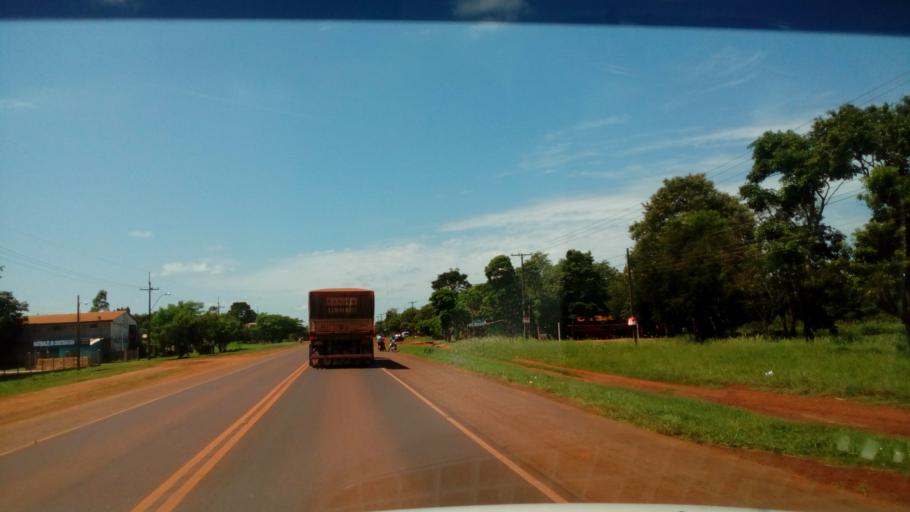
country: PY
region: Alto Parana
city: Colonia Yguazu
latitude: -25.4988
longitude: -54.8984
